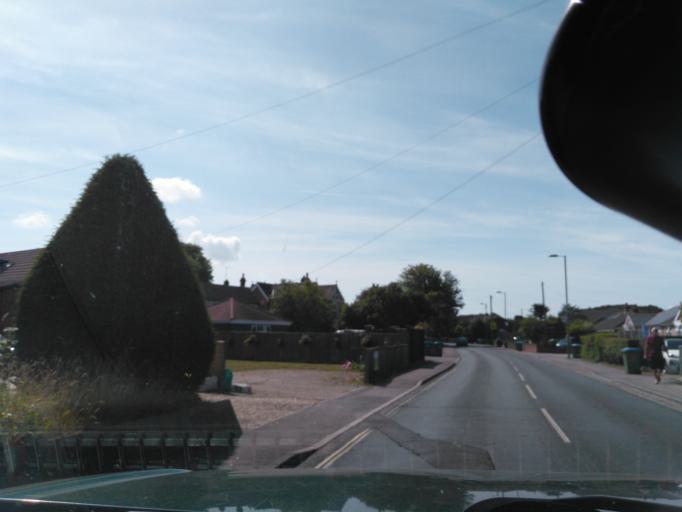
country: GB
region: England
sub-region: Hampshire
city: Lee-on-the-Solent
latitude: 50.8282
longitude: -1.2164
